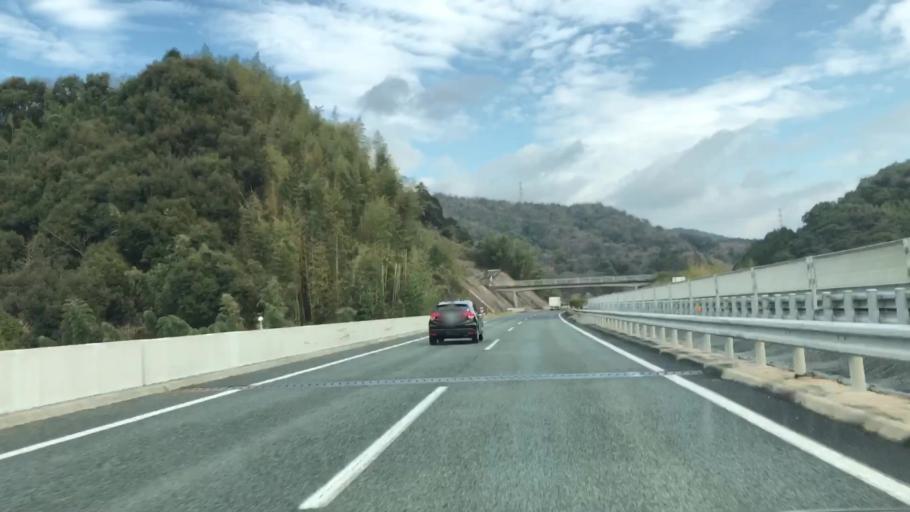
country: JP
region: Saga Prefecture
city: Kanzakimachi-kanzaki
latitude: 33.3358
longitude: 130.3274
